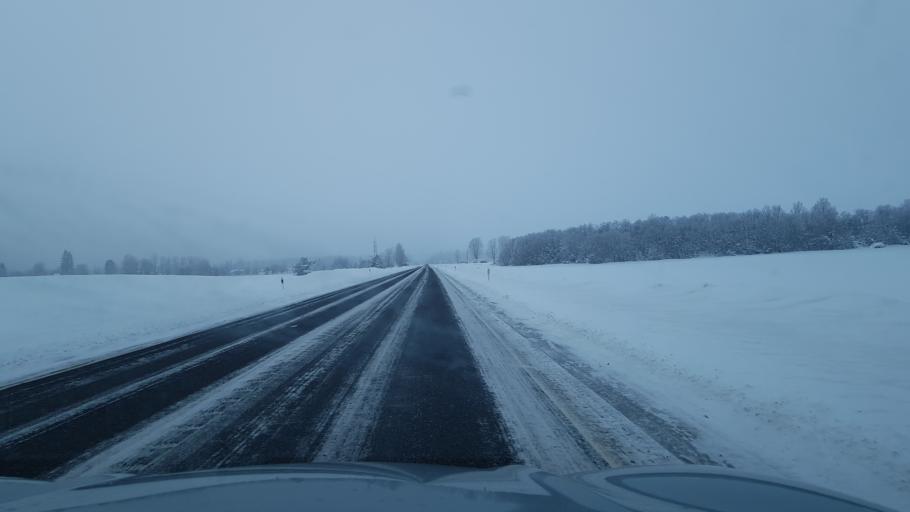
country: EE
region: Ida-Virumaa
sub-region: Johvi vald
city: Johvi
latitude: 59.2448
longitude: 27.3651
